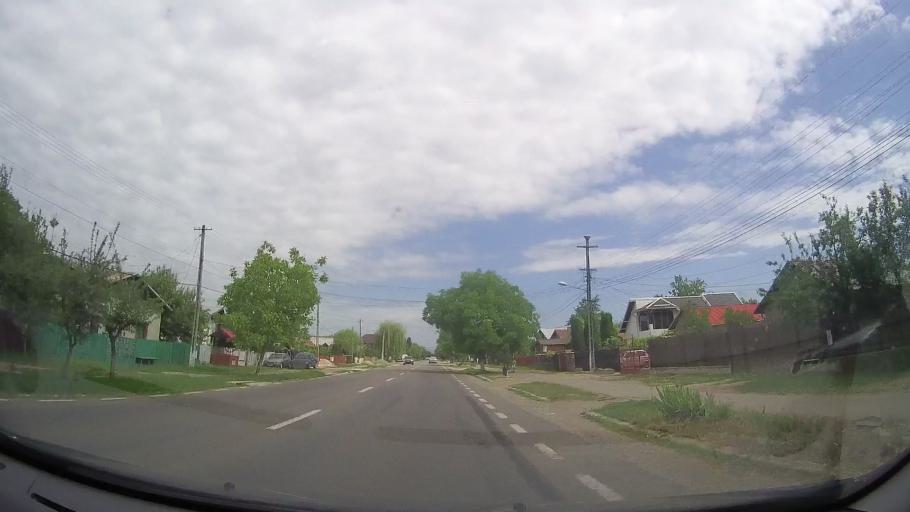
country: RO
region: Prahova
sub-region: Comuna Lipanesti
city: Lipanesti
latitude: 45.0517
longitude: 26.0197
